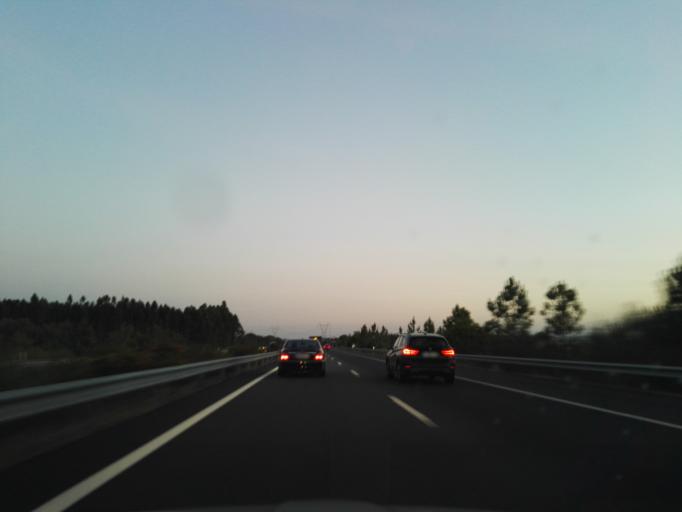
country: PT
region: Setubal
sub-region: Alcacer do Sal
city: Alcacer do Sal
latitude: 38.4525
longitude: -8.5263
